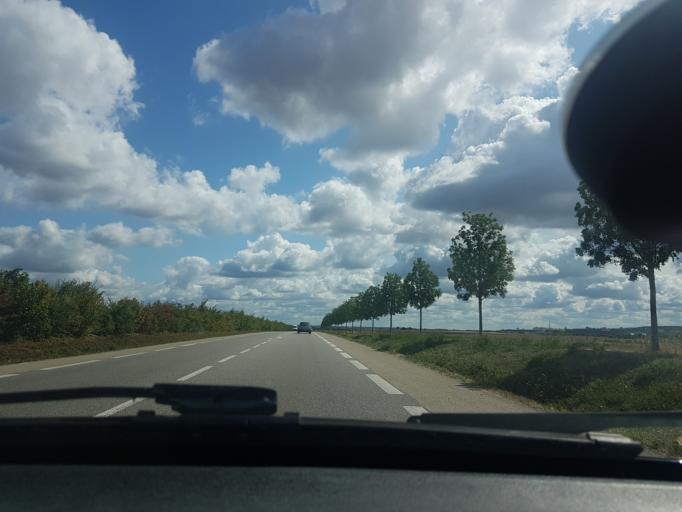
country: FR
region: Ile-de-France
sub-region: Departement des Yvelines
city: Plaisir
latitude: 48.8348
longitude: 1.9605
